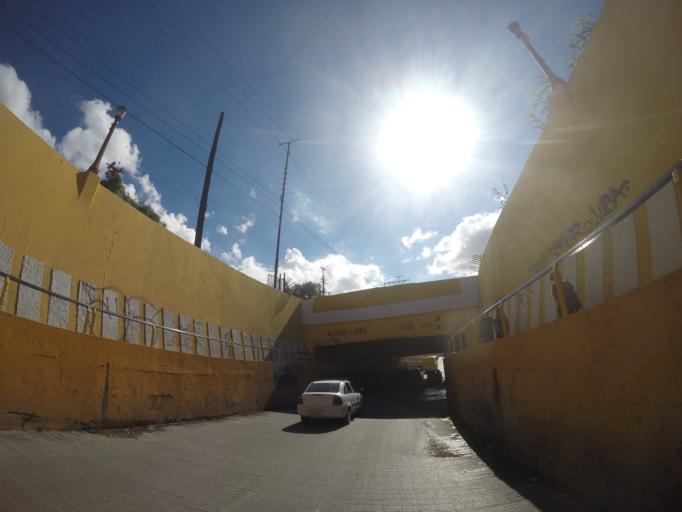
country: MX
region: San Luis Potosi
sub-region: San Luis Potosi
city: San Luis Potosi
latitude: 22.1535
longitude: -100.9681
